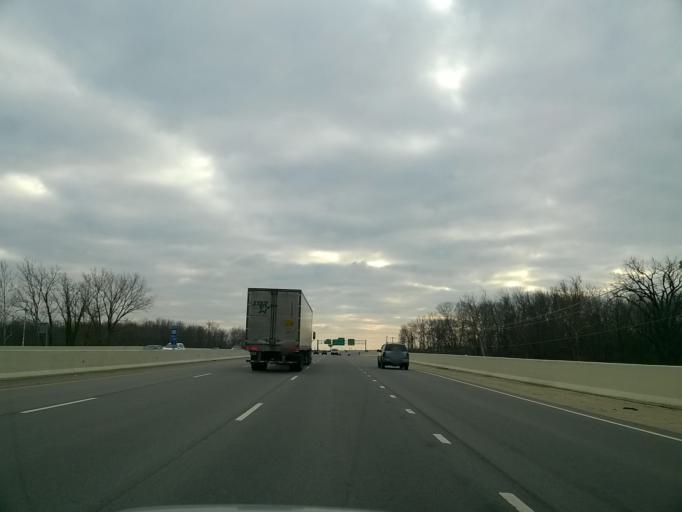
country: US
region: Indiana
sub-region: Hamilton County
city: Westfield
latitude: 40.0135
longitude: -86.1289
